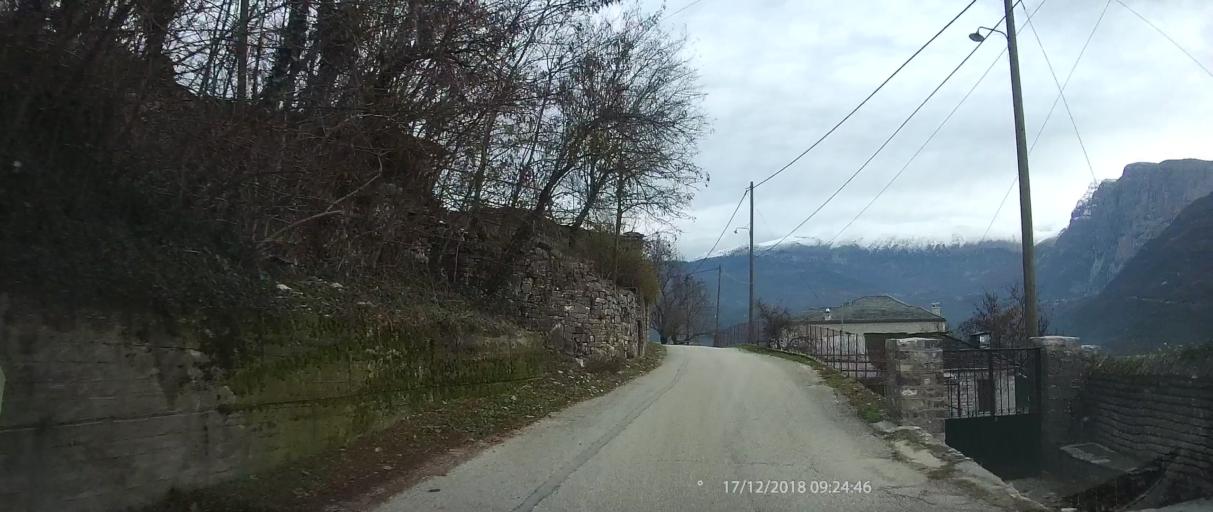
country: GR
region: Epirus
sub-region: Nomos Ioanninon
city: Kalpaki
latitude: 39.9357
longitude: 20.6727
